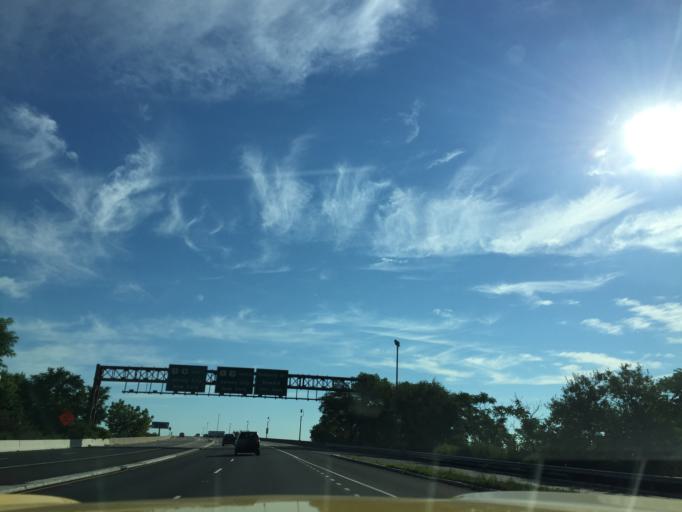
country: US
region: New Jersey
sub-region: Essex County
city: Newark
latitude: 40.7106
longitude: -74.1587
